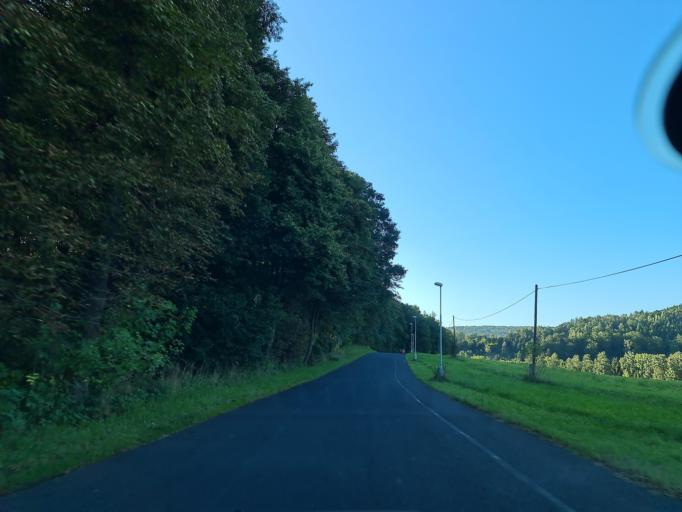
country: DE
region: Saxony
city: Olbernhau
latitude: 50.6457
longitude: 13.3755
